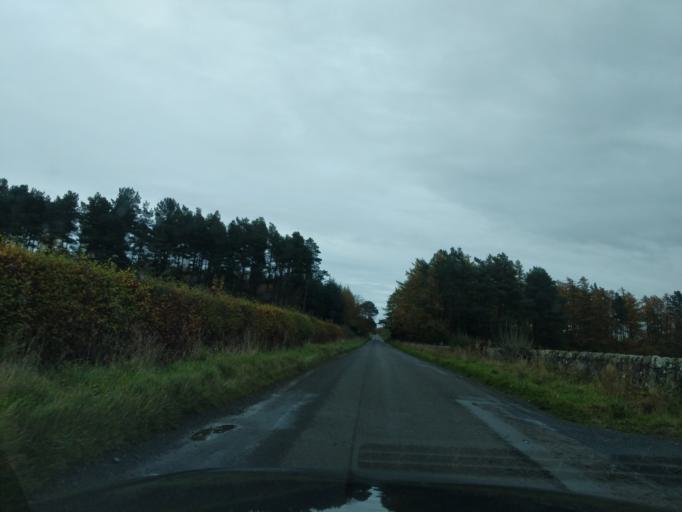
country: GB
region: Scotland
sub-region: Fife
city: Saint Andrews
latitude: 56.2879
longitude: -2.8169
